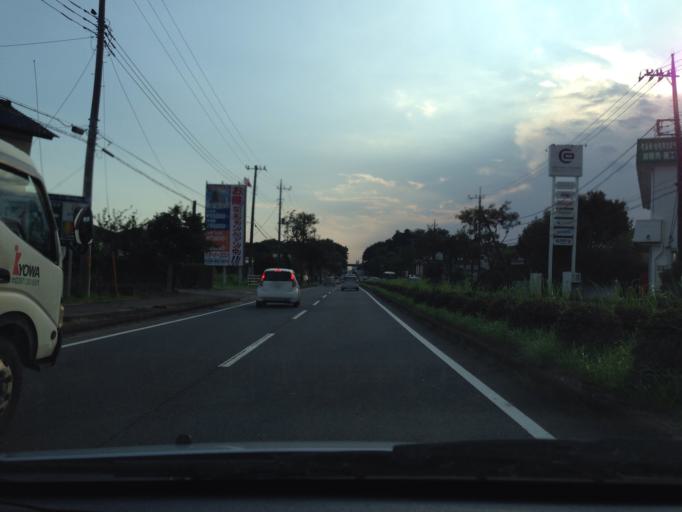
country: JP
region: Ibaraki
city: Naka
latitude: 36.0909
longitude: 140.1392
